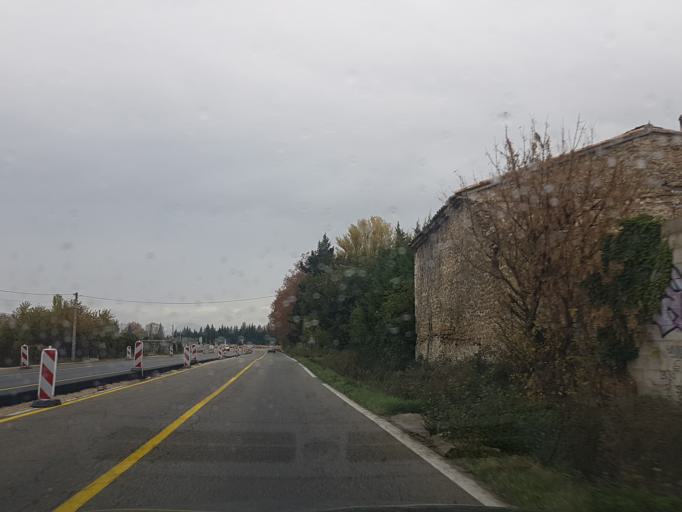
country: FR
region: Provence-Alpes-Cote d'Azur
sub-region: Departement du Vaucluse
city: Althen-des-Paluds
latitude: 44.0245
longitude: 4.9660
